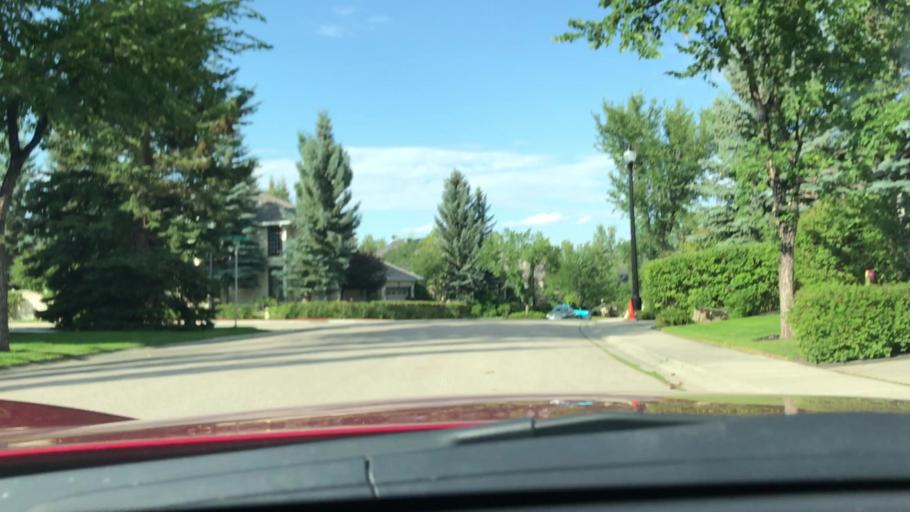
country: CA
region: Alberta
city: Calgary
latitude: 51.0256
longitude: -114.1741
